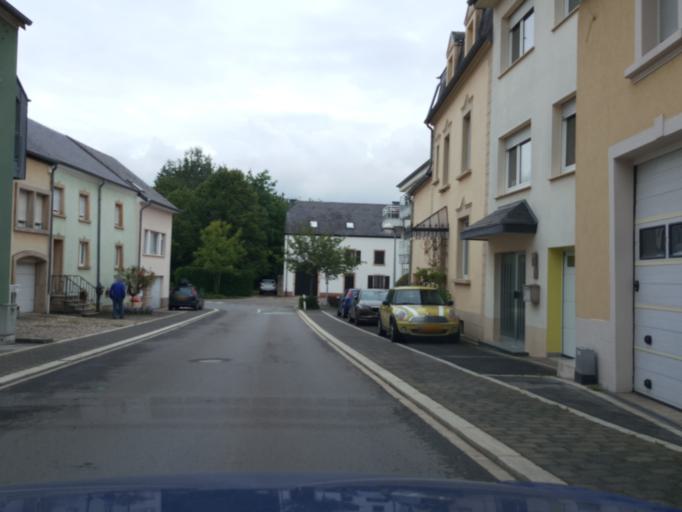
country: LU
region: Luxembourg
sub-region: Canton de Capellen
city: Mamer
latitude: 49.6269
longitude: 6.0234
